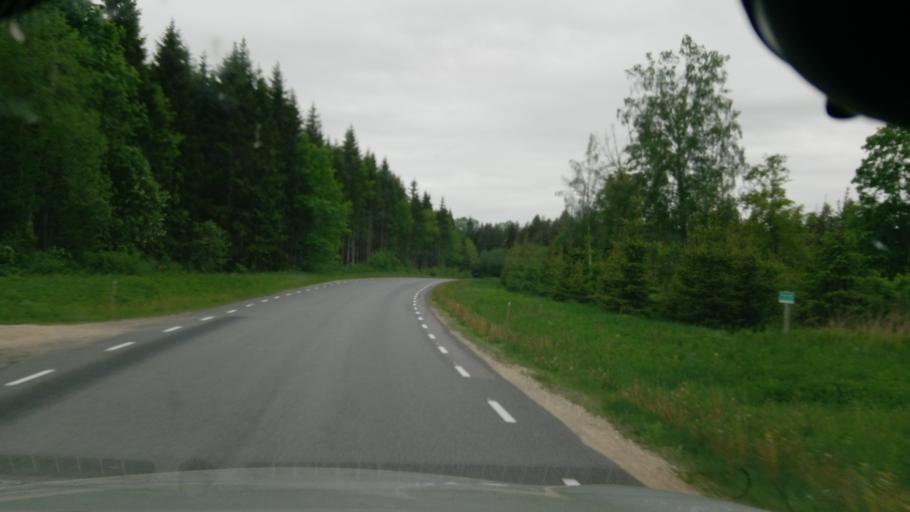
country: EE
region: Jaervamaa
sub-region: Koeru vald
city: Koeru
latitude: 58.9895
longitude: 26.0546
